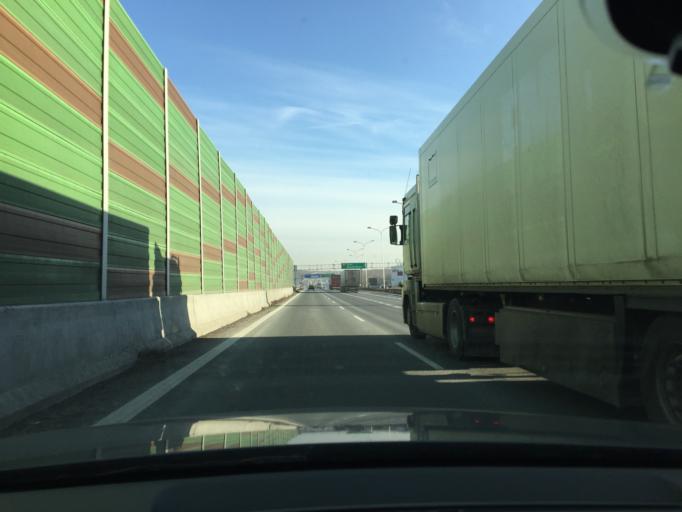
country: PL
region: Silesian Voivodeship
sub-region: Katowice
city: Katowice
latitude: 50.2451
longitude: 19.0341
